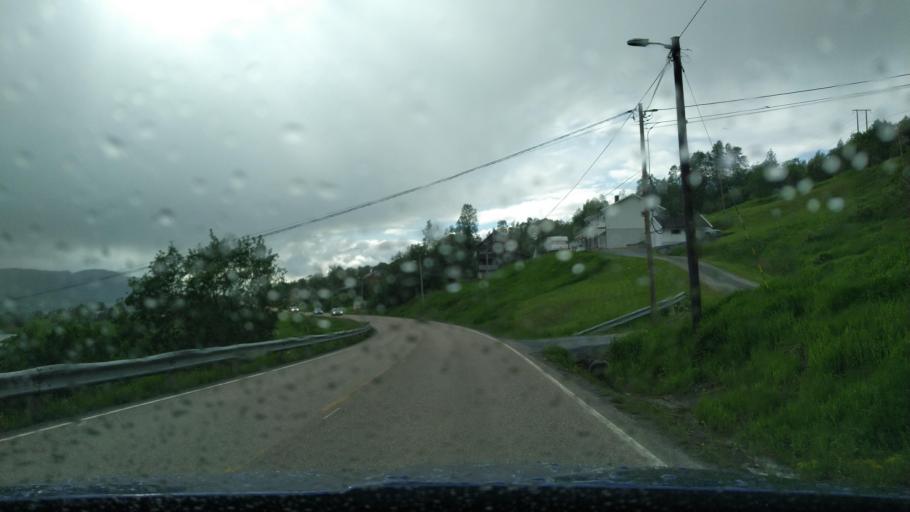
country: NO
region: Troms
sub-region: Sorreisa
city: Sorreisa
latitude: 69.1608
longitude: 18.1439
